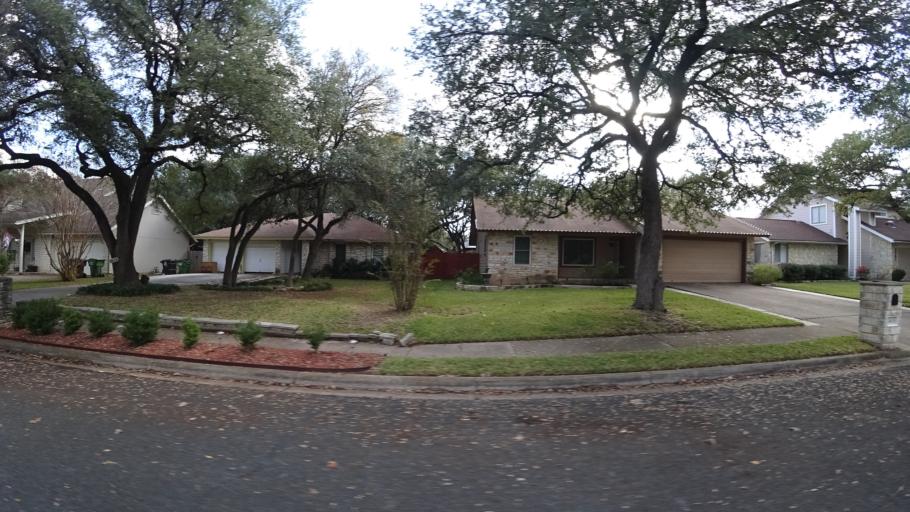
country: US
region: Texas
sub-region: Williamson County
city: Brushy Creek
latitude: 30.5098
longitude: -97.7345
